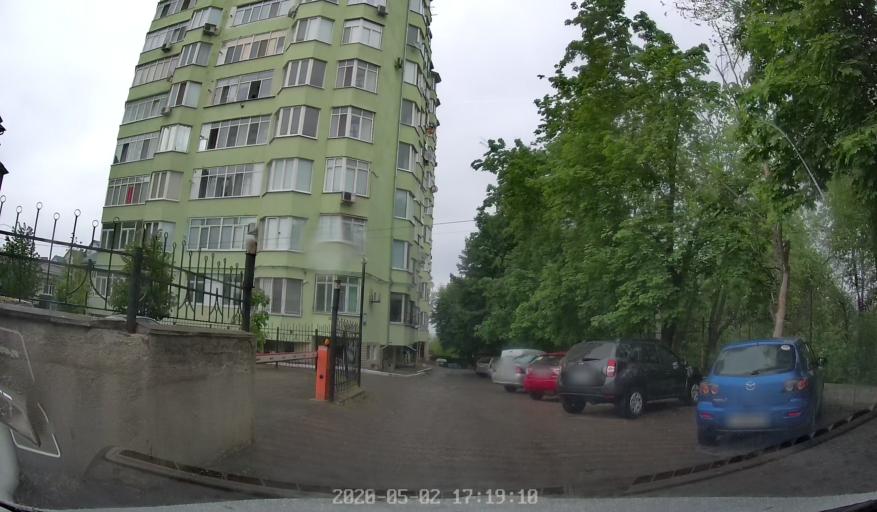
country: MD
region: Chisinau
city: Chisinau
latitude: 46.9892
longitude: 28.8308
